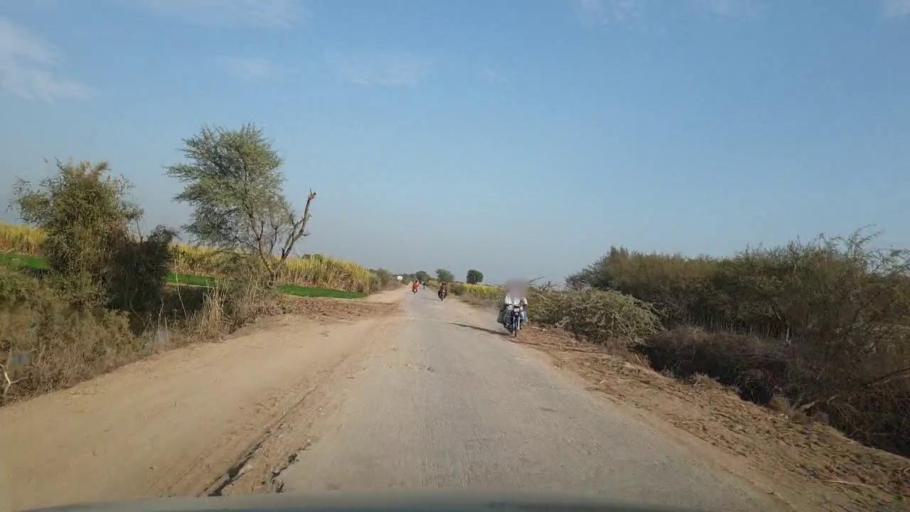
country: PK
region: Sindh
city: Tando Allahyar
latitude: 25.5936
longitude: 68.6803
